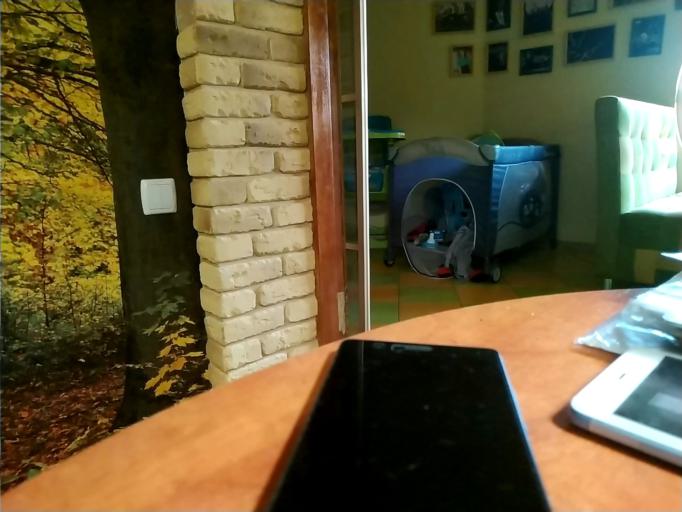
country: RU
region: Kaluga
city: Duminichi
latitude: 53.7189
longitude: 35.4242
